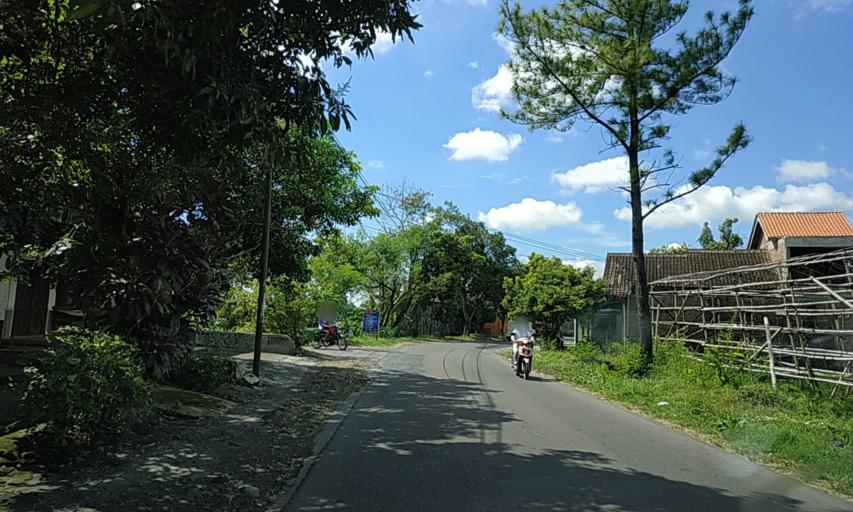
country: ID
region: Central Java
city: Trucuk
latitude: -7.6962
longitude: 110.6530
